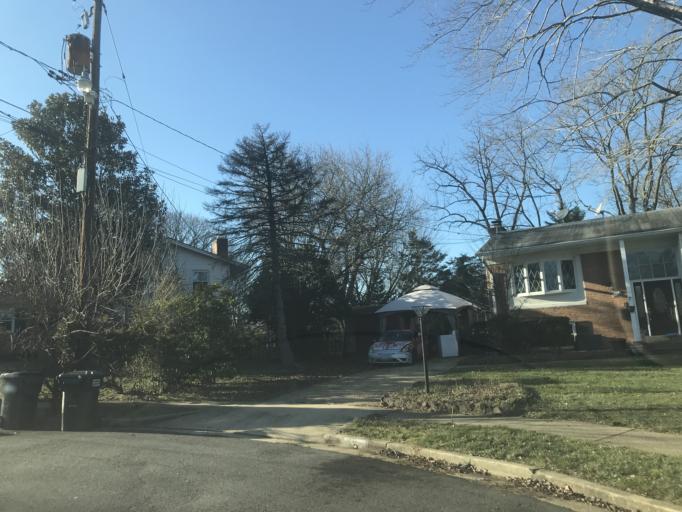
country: US
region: Virginia
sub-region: Fairfax County
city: Franconia
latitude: 38.7855
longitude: -77.1636
